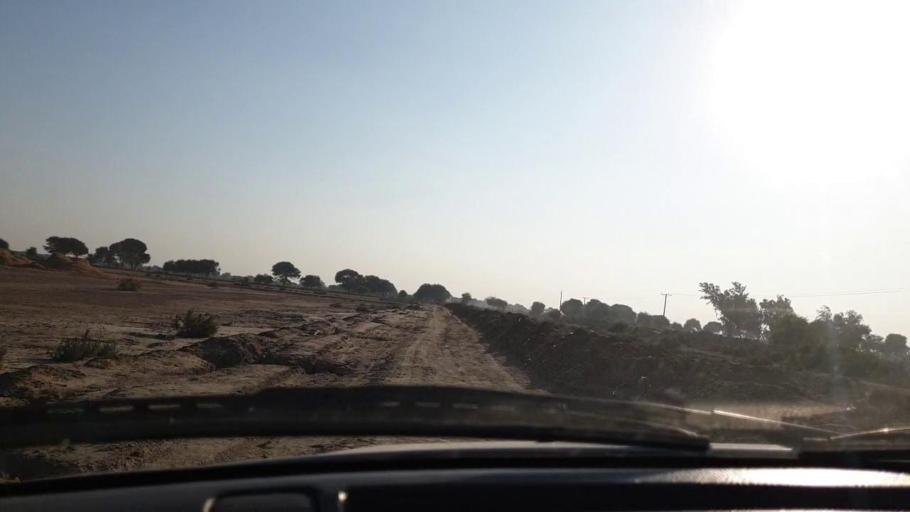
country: PK
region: Sindh
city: Bulri
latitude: 24.8103
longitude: 68.3980
